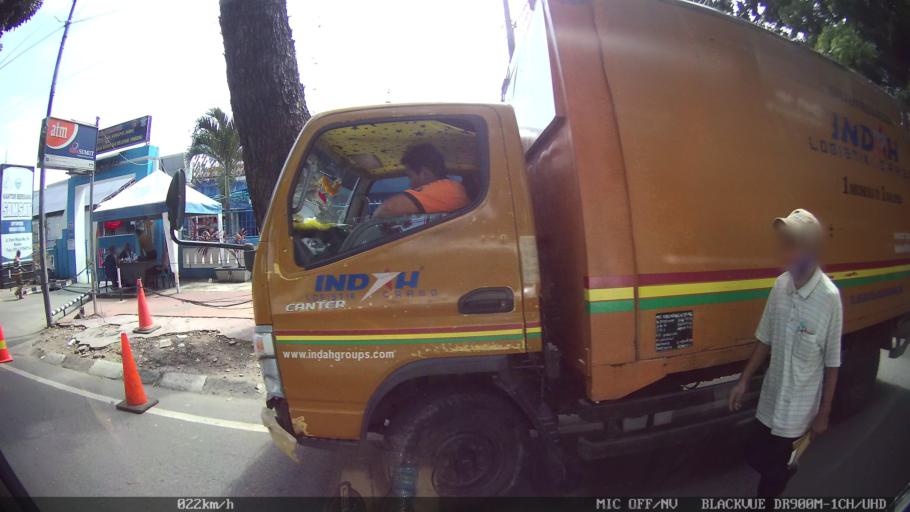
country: ID
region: North Sumatra
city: Medan
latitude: 3.5971
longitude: 98.6752
